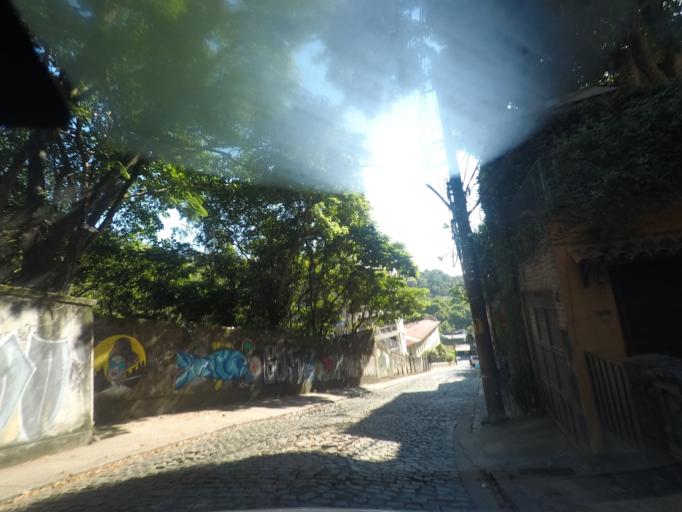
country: BR
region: Rio de Janeiro
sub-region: Rio De Janeiro
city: Rio de Janeiro
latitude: -22.9403
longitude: -43.2041
